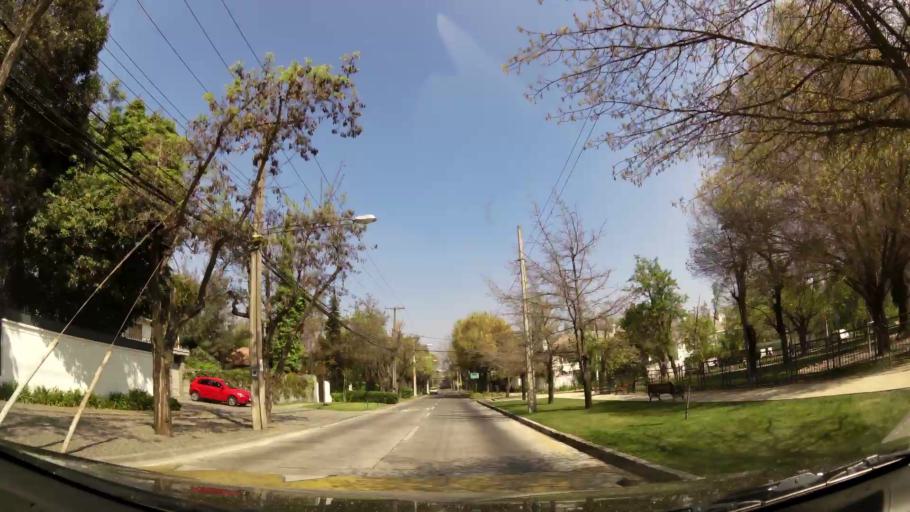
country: CL
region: Santiago Metropolitan
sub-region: Provincia de Santiago
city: Villa Presidente Frei, Nunoa, Santiago, Chile
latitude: -33.3960
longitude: -70.5949
